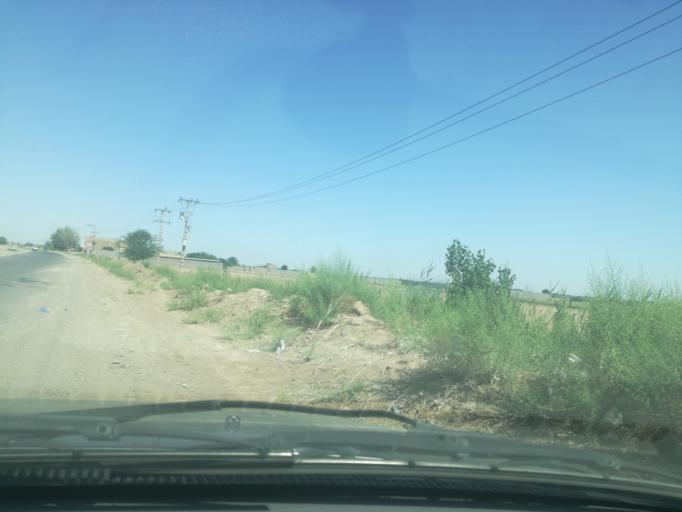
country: IR
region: Razavi Khorasan
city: Sarakhs
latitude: 36.5617
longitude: 61.1478
